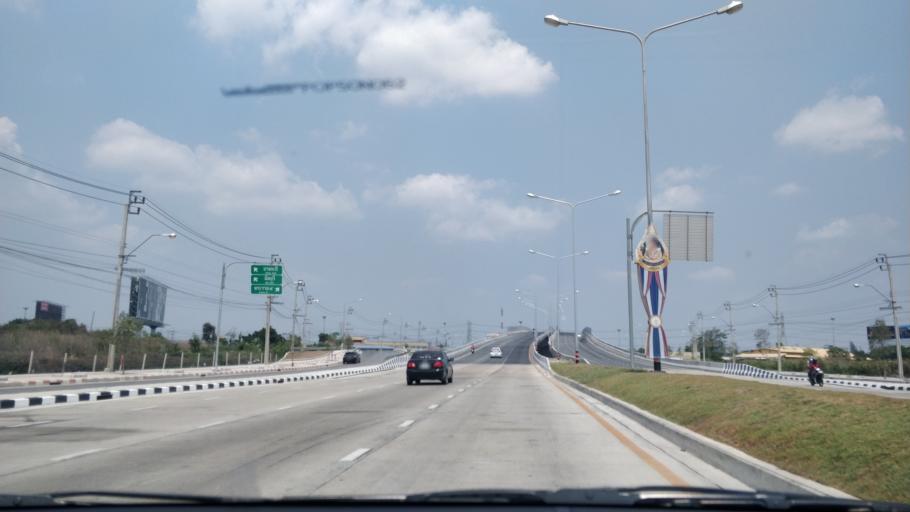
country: TH
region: Bangkok
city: Saphan Sung
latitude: 13.7529
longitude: 100.6964
